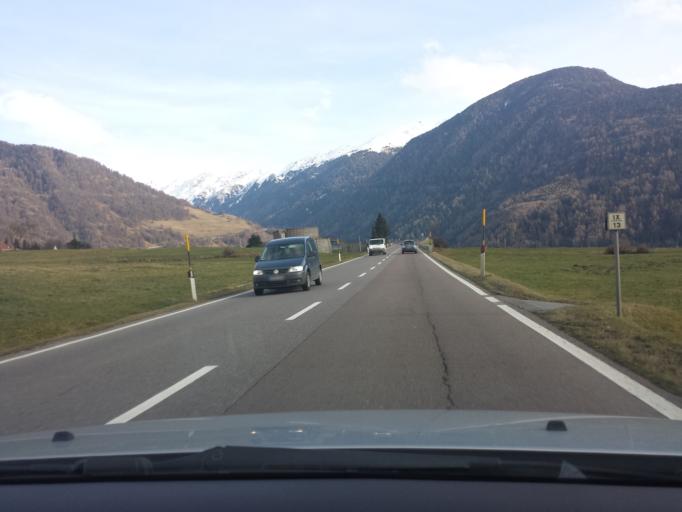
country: IT
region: Trentino-Alto Adige
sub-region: Bolzano
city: Malles Venosta
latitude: 46.7165
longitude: 10.5339
